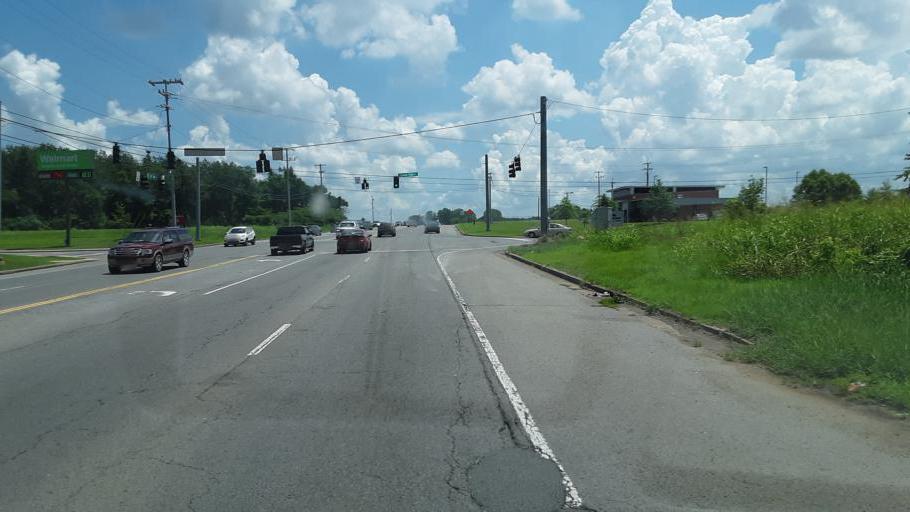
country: US
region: Kentucky
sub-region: Christian County
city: Oak Grove
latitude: 36.6329
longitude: -87.4234
